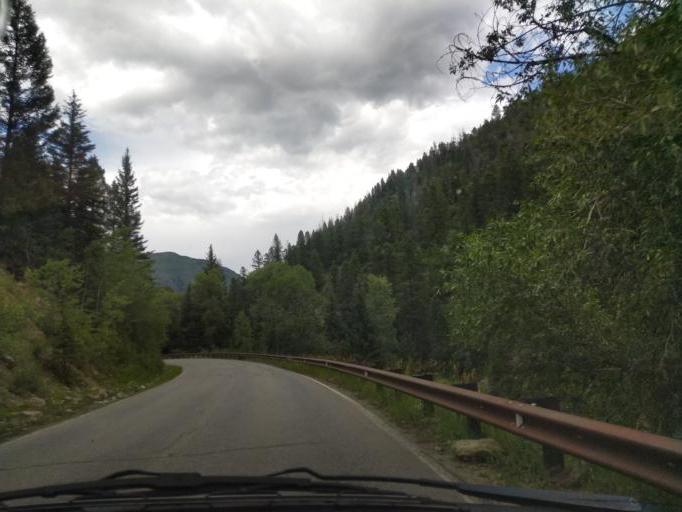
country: US
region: Colorado
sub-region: Garfield County
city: Carbondale
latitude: 39.1062
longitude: -107.2650
